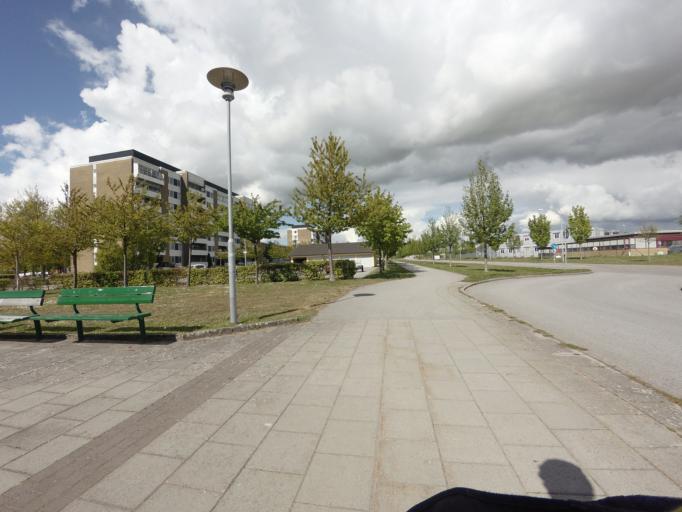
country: SE
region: Skane
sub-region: Landskrona
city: Landskrona
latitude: 55.8901
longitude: 12.8506
